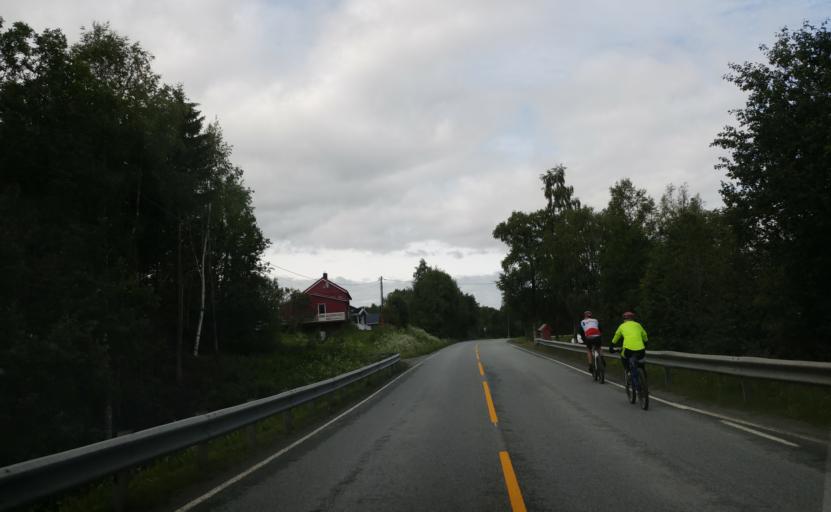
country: NO
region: Nord-Trondelag
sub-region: Stjordal
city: Stjordalshalsen
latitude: 63.4016
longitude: 10.9454
